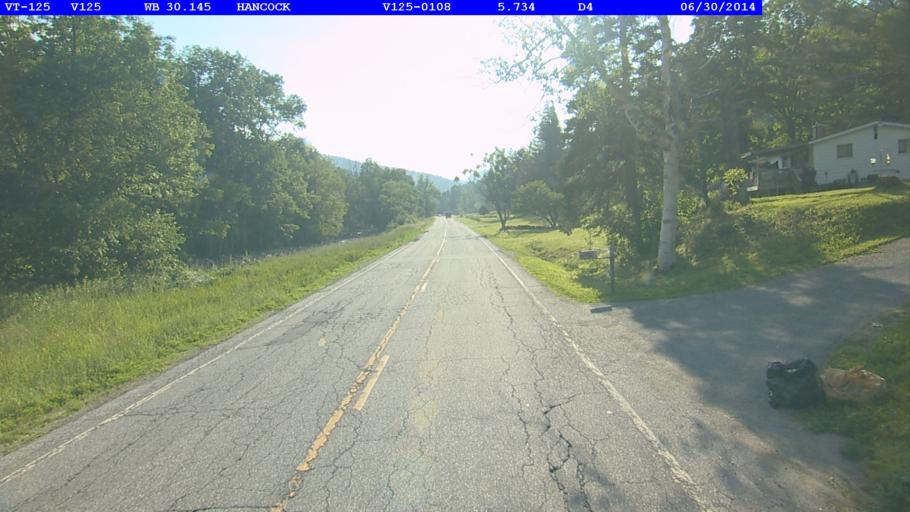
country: US
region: Vermont
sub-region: Orange County
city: Randolph
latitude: 43.9268
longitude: -72.8691
